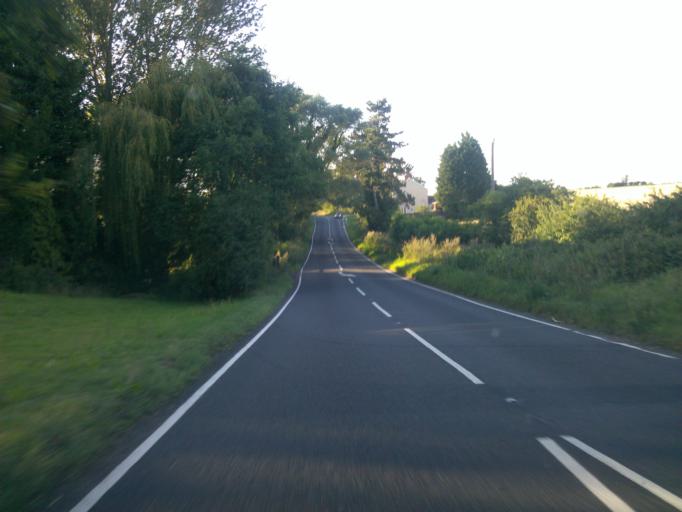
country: GB
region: England
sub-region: Essex
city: Saint Osyth
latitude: 51.8207
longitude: 1.0703
